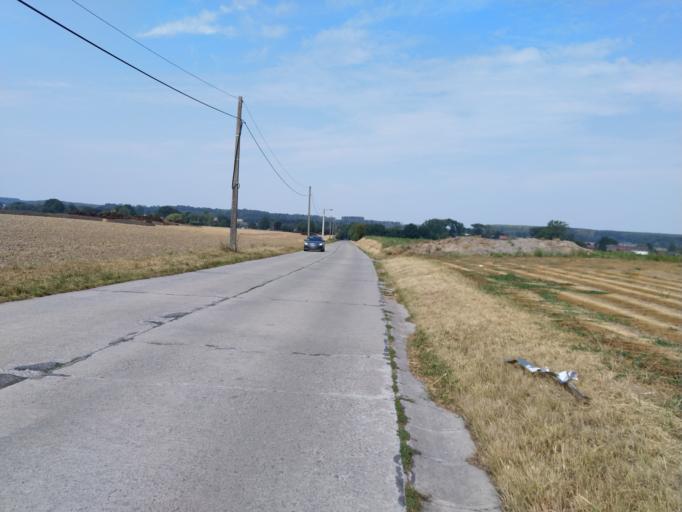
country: BE
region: Wallonia
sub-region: Province du Hainaut
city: Soignies
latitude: 50.5206
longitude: 4.0418
